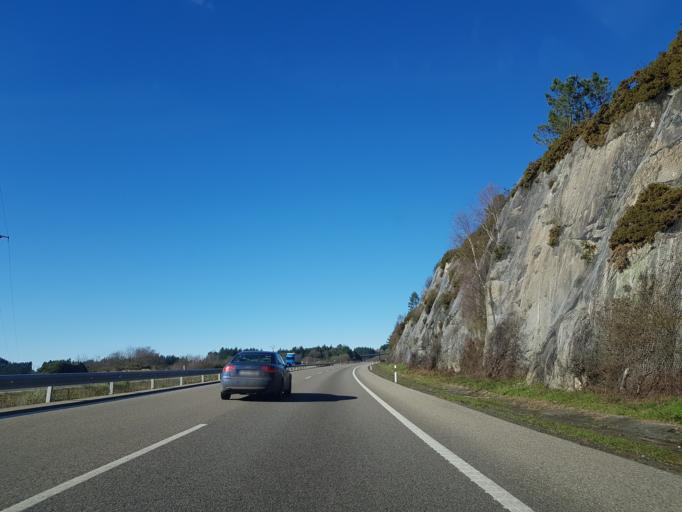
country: ES
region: Galicia
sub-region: Provincia de Lugo
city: Guitiriz
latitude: 43.1744
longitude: -7.7964
